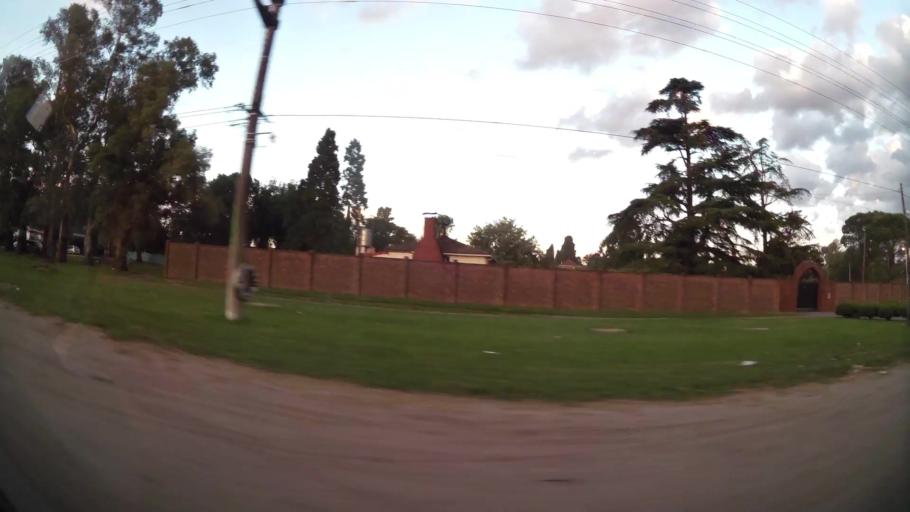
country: AR
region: Buenos Aires
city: Santa Catalina - Dique Lujan
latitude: -34.4799
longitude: -58.7802
